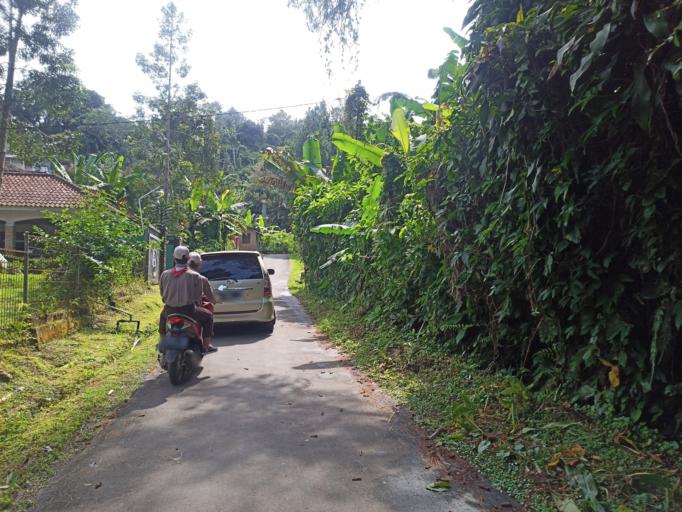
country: ID
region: West Java
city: Caringin
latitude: -6.6460
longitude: 106.9117
